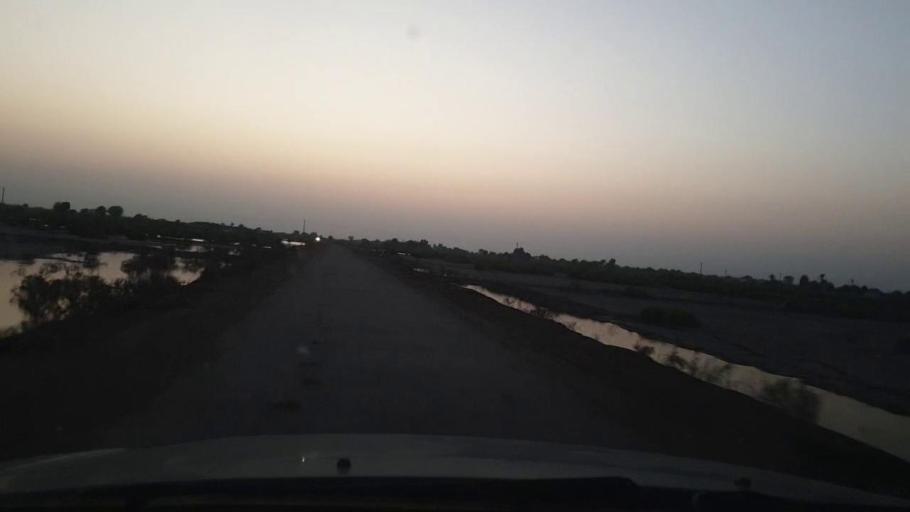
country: PK
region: Sindh
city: Tando Ghulam Ali
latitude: 25.1150
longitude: 68.9837
